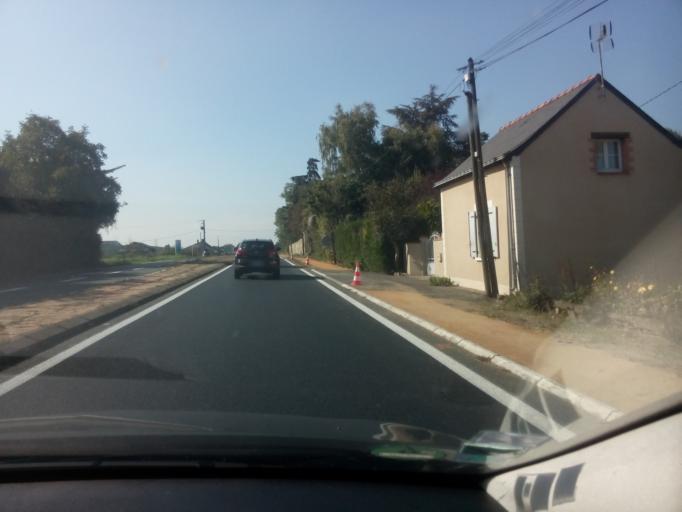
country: FR
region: Pays de la Loire
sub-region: Departement de Maine-et-Loire
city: Corze
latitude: 47.5576
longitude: -0.3773
